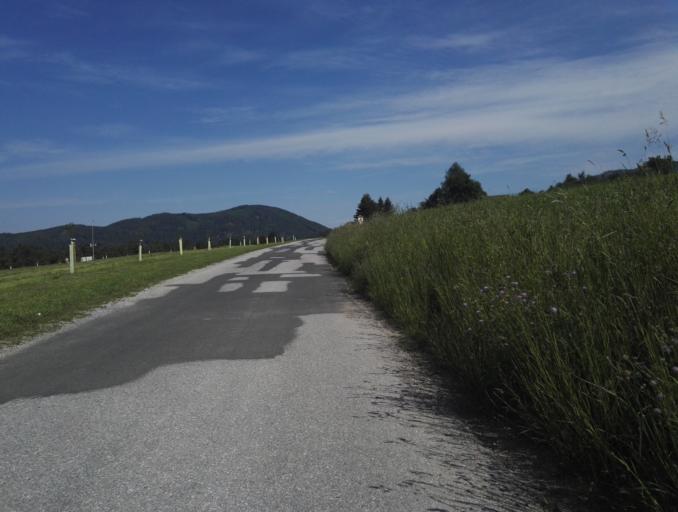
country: AT
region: Styria
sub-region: Politischer Bezirk Graz-Umgebung
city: Stattegg
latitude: 47.1439
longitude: 15.4349
